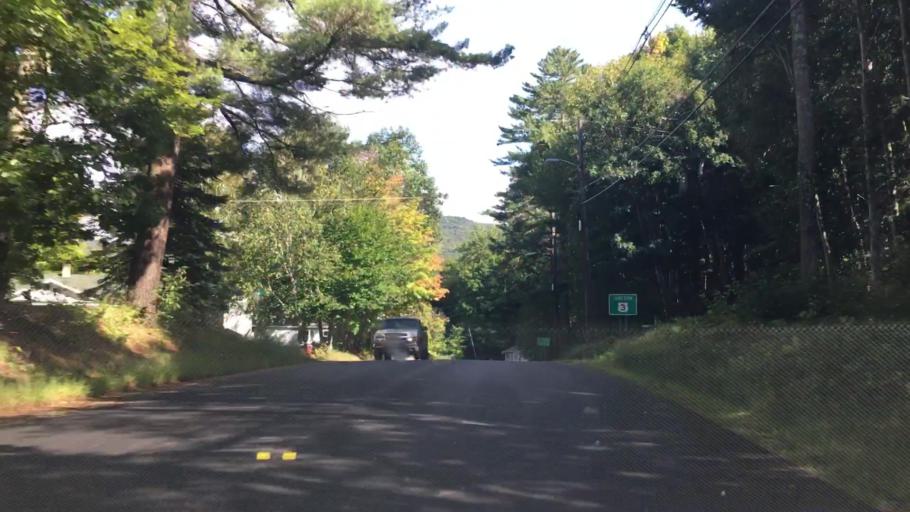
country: US
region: New Hampshire
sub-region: Grafton County
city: Woodstock
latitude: 44.0307
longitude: -71.6893
